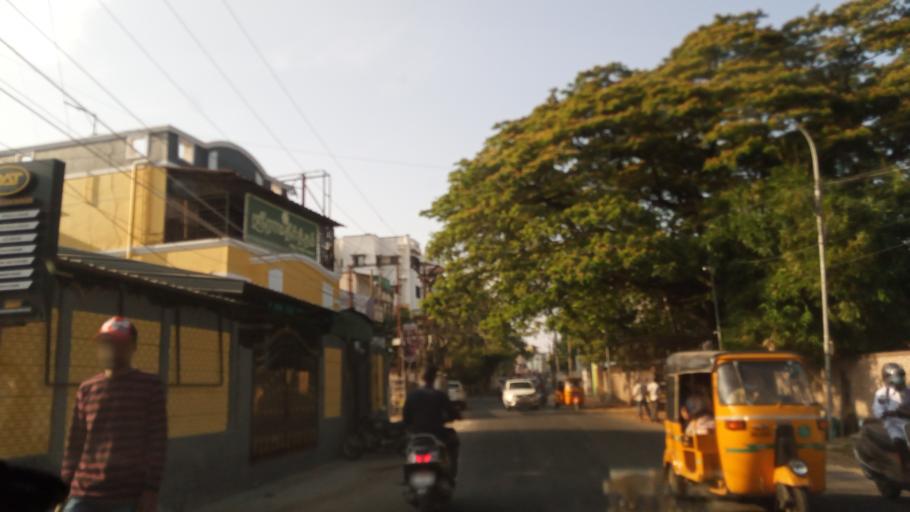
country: IN
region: Tamil Nadu
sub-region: Kancheepuram
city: Manappakkam
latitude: 13.0247
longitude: 80.1831
